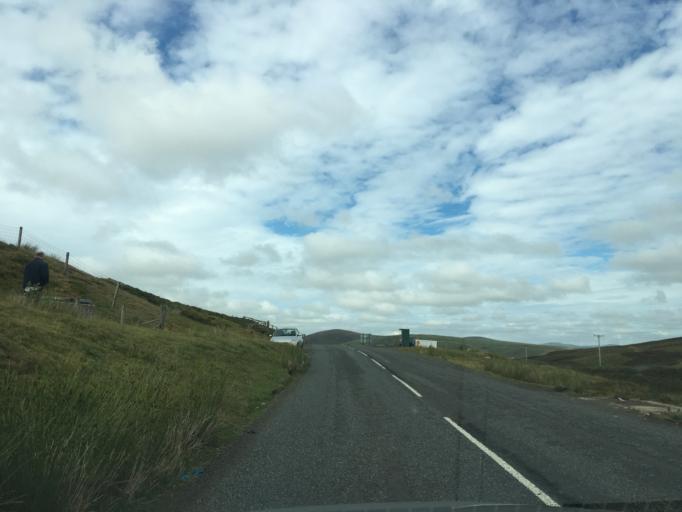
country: GB
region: Scotland
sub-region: Dumfries and Galloway
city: Sanquhar
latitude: 55.4014
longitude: -3.7704
